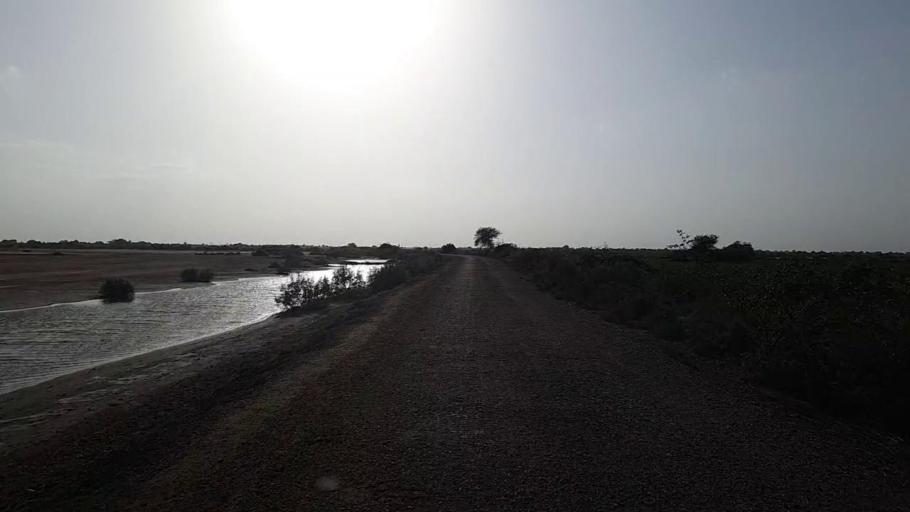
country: PK
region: Sindh
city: Mirpur Batoro
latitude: 24.6679
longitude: 68.4527
